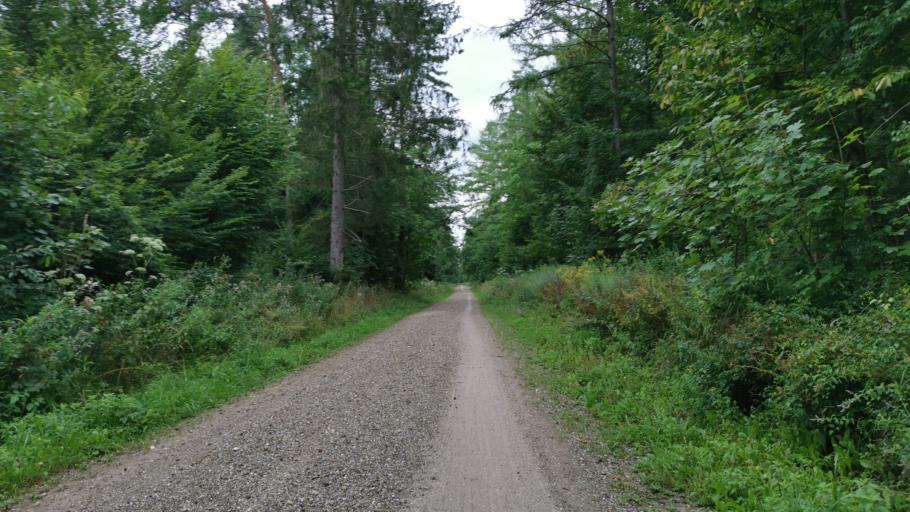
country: DE
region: Bavaria
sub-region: Upper Bavaria
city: Pullach im Isartal
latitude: 48.0744
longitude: 11.5578
